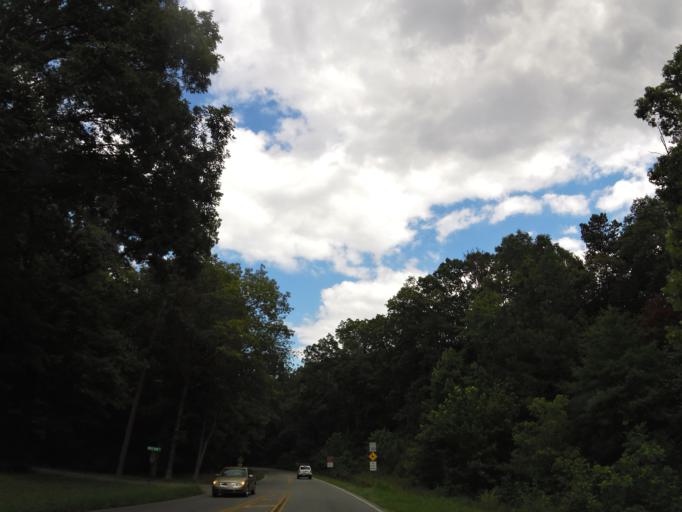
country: US
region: Georgia
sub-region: Walker County
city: Fairview
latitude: 34.9413
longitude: -85.2748
